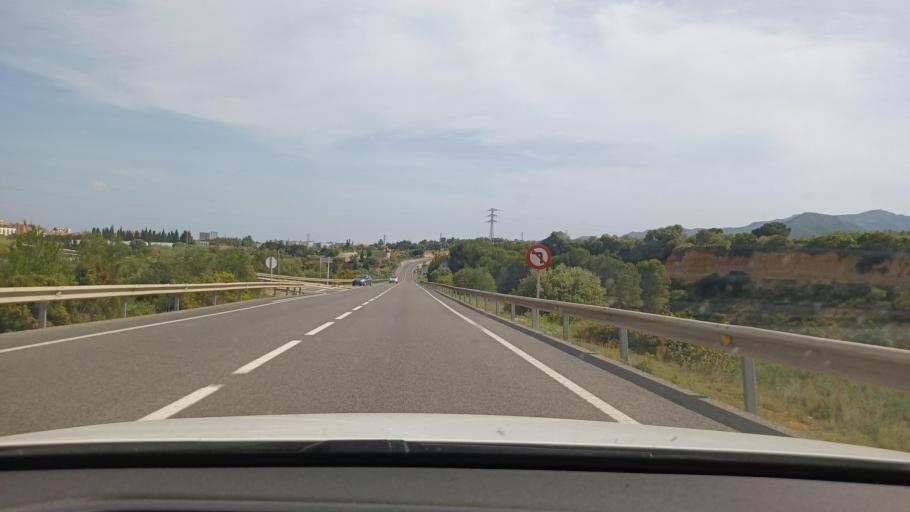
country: ES
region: Catalonia
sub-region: Provincia de Tarragona
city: Amposta
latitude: 40.7150
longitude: 0.5637
